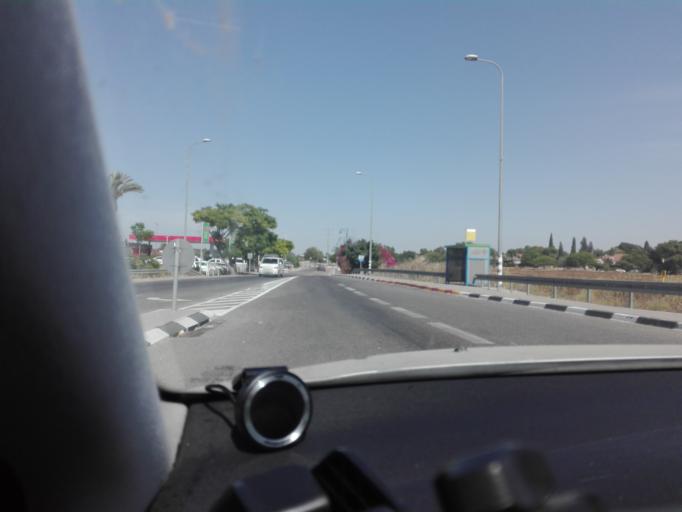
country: IL
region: Central District
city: Bene 'Ayish
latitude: 31.7188
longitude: 34.7543
